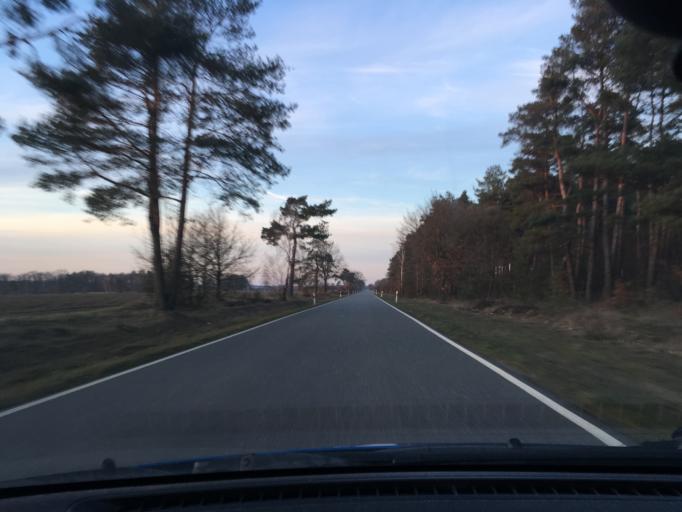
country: DE
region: Schleswig-Holstein
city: Langenlehsten
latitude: 53.5164
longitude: 10.7446
